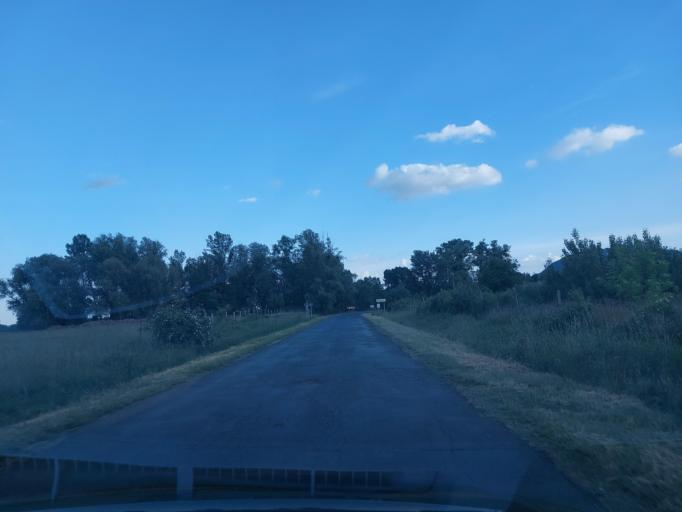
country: HU
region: Veszprem
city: Devecser
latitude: 47.1803
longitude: 17.3633
